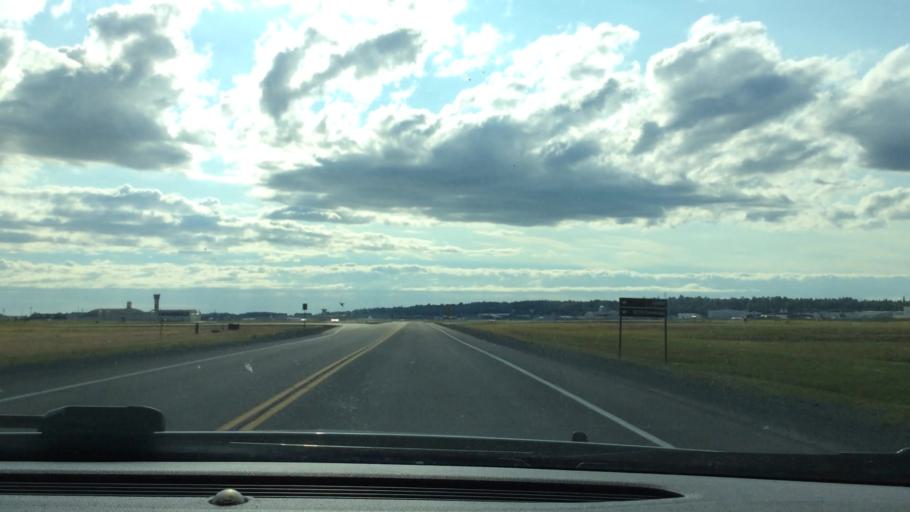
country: US
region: Alaska
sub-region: Anchorage Municipality
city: Anchorage
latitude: 61.2532
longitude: -149.7778
